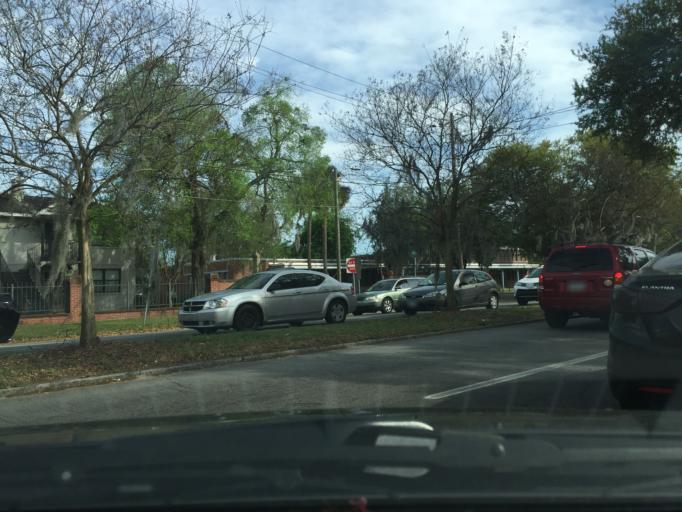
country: US
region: Georgia
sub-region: Chatham County
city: Savannah
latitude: 32.0758
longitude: -81.0853
